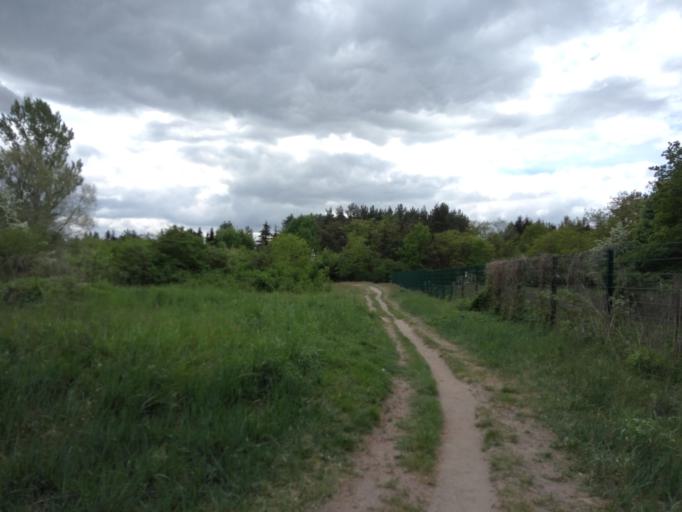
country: DE
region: Berlin
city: Kaulsdorf
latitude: 52.4915
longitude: 13.5898
